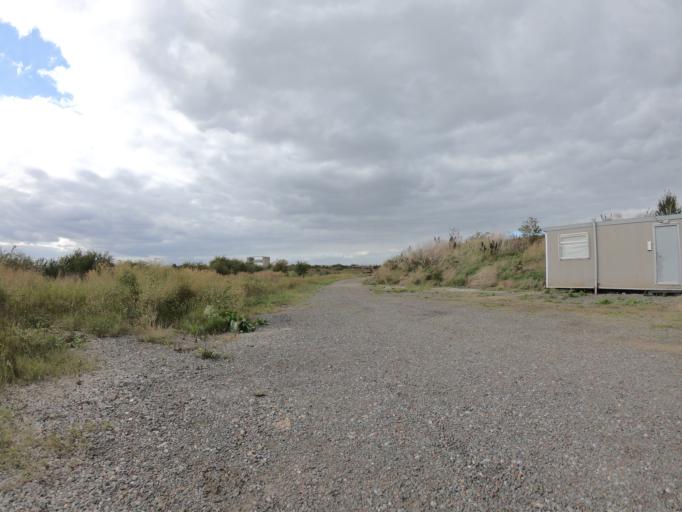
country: GB
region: England
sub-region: Essex
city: Purfleet
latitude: 51.4748
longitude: 0.2228
